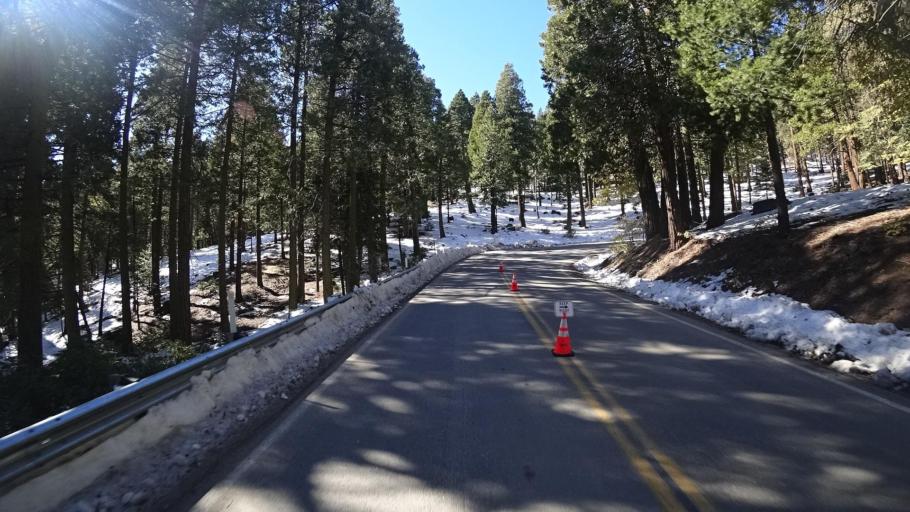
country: US
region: California
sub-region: Kern County
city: Alta Sierra
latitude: 35.7372
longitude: -118.5559
